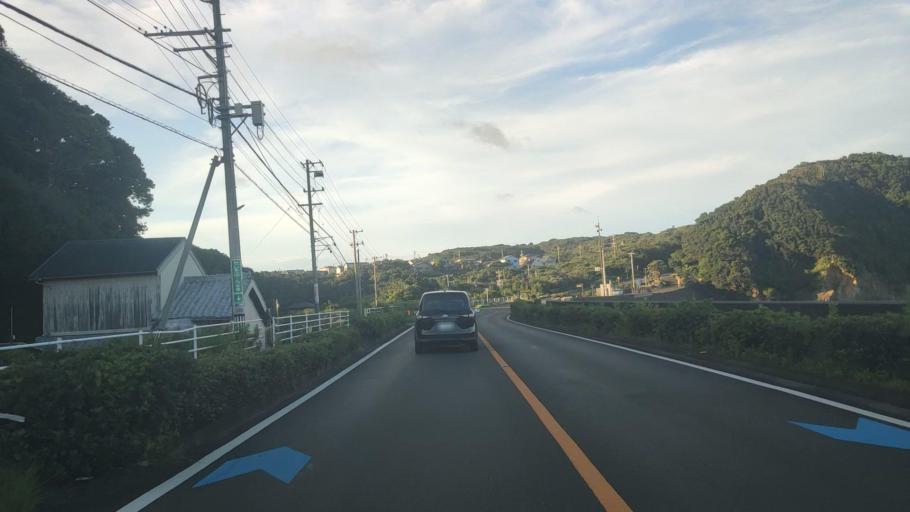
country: JP
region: Mie
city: Toba
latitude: 34.2728
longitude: 136.8688
